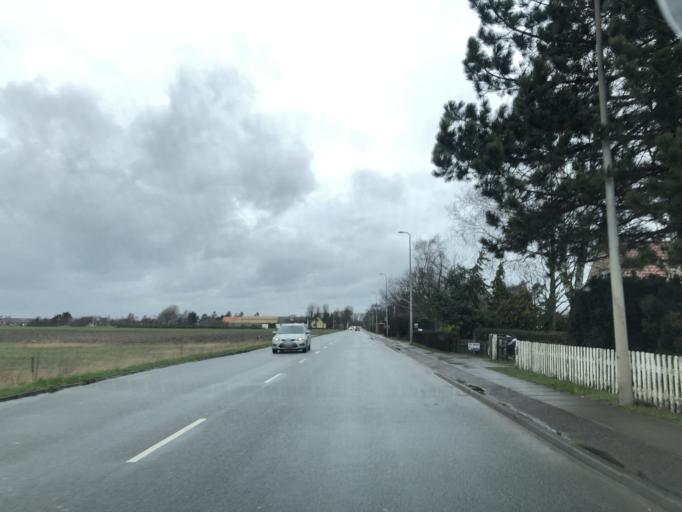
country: DK
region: Capital Region
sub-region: Dragor Kommune
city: Dragor
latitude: 55.5877
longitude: 12.6356
